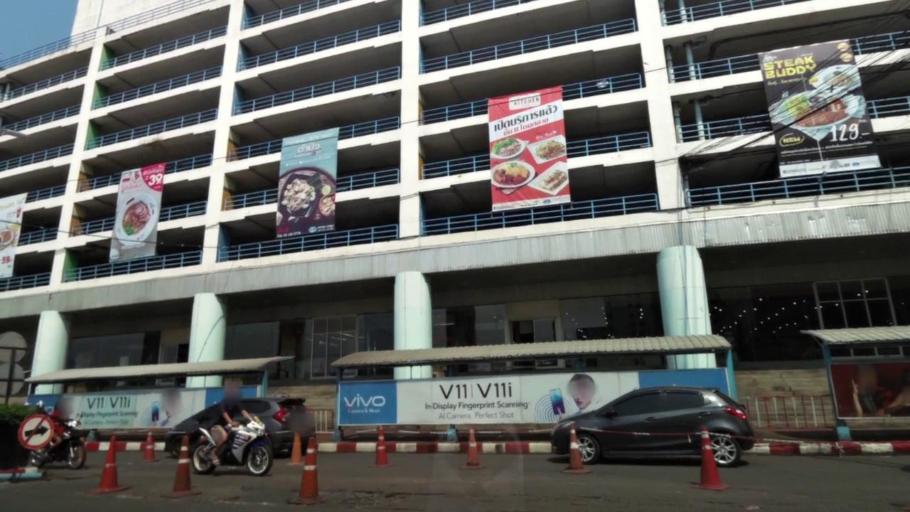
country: TH
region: Bangkok
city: Bang Na
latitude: 13.6501
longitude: 100.5949
